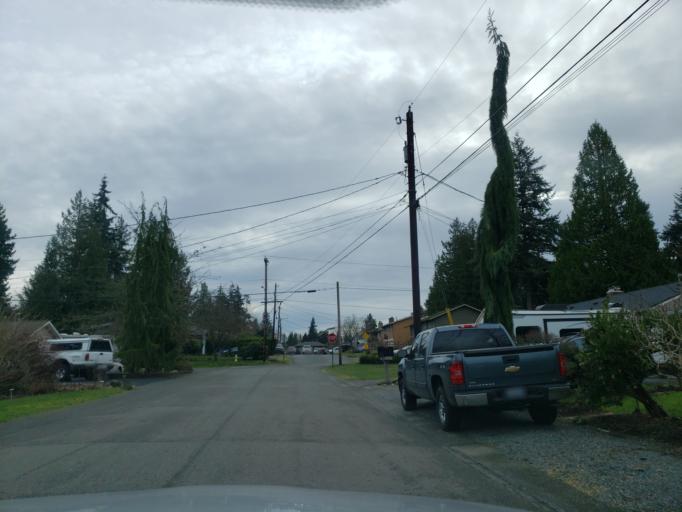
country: US
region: Washington
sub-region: Snohomish County
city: Esperance
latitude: 47.8128
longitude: -122.3423
